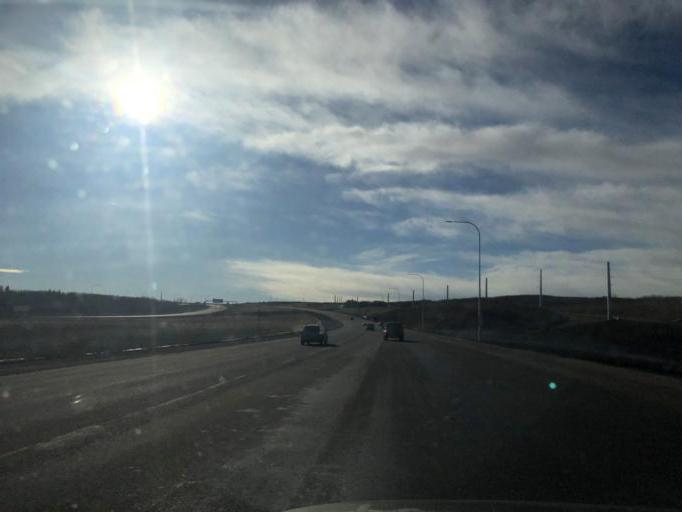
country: CA
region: Alberta
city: Calgary
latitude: 50.9918
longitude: -114.1680
